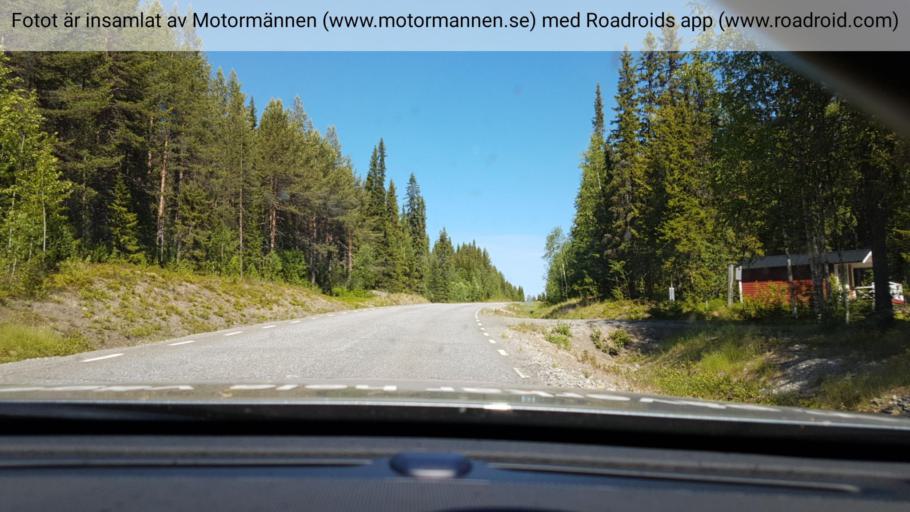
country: SE
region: Vaesterbotten
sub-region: Vilhelmina Kommun
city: Sjoberg
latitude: 64.9052
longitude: 15.8638
